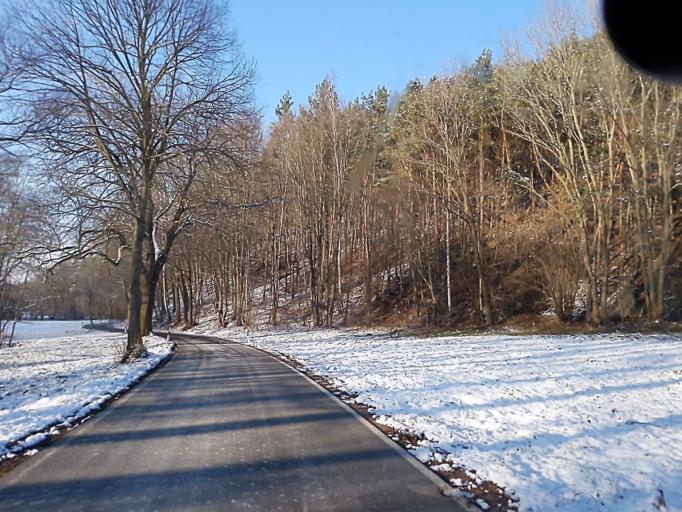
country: DE
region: Saxony
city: Hartha
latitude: 51.1442
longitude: 12.9832
